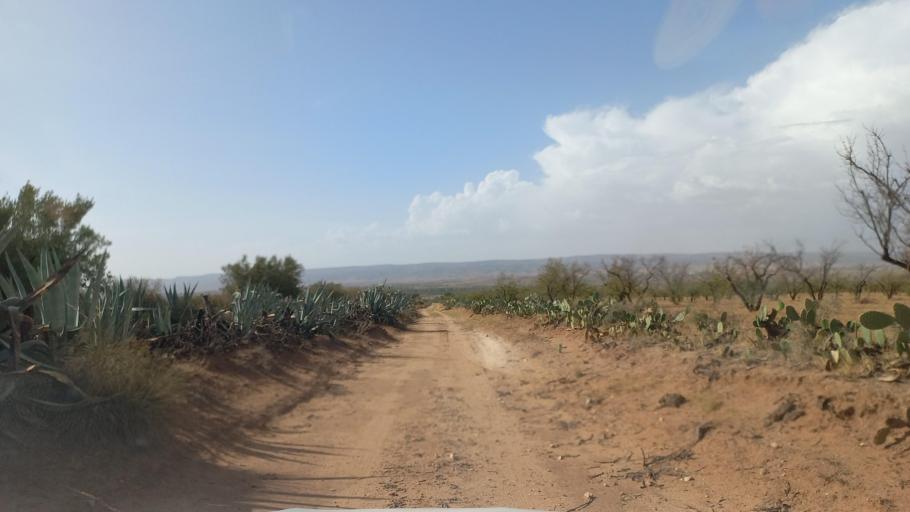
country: TN
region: Al Qasrayn
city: Kasserine
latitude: 35.2075
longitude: 8.9581
